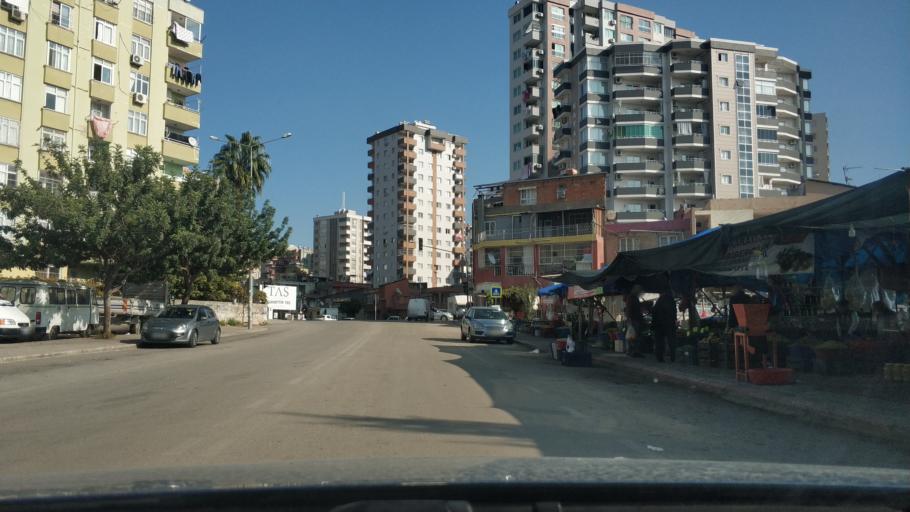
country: TR
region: Adana
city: Seyhan
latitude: 37.0225
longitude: 35.2915
